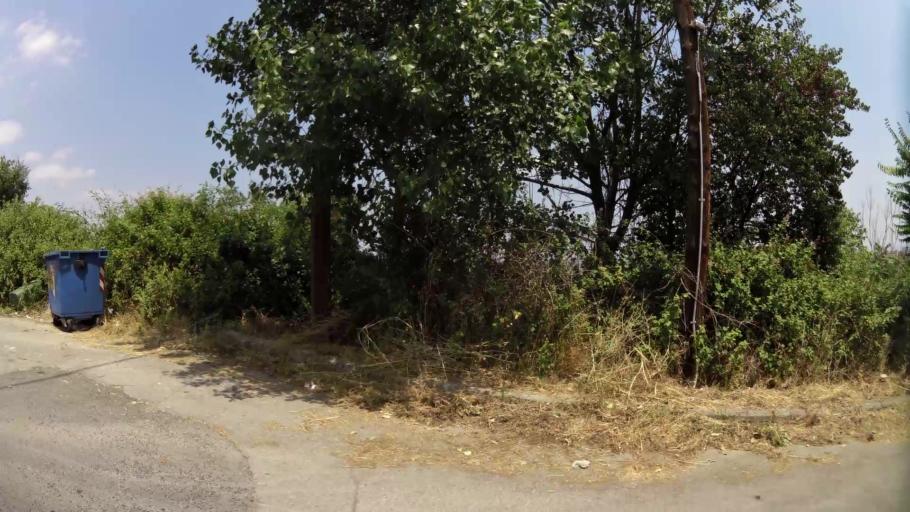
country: GR
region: Central Macedonia
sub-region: Nomos Imathias
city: Veroia
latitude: 40.5156
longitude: 22.1871
